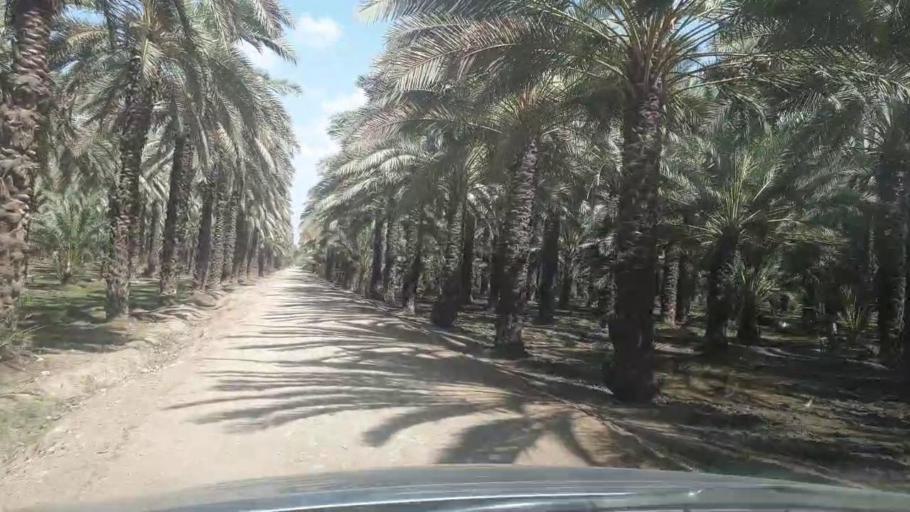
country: PK
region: Sindh
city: Khairpur
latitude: 27.5504
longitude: 68.7919
